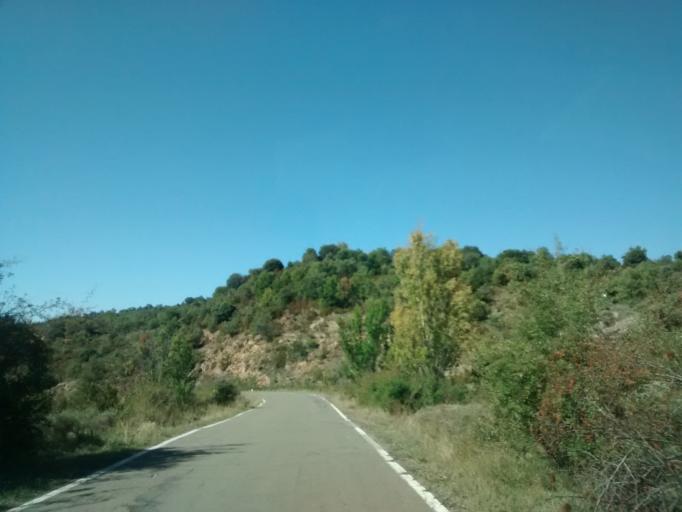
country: ES
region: Aragon
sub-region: Provincia de Huesca
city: Santa Cruz de la Seros
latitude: 42.4772
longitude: -0.5926
